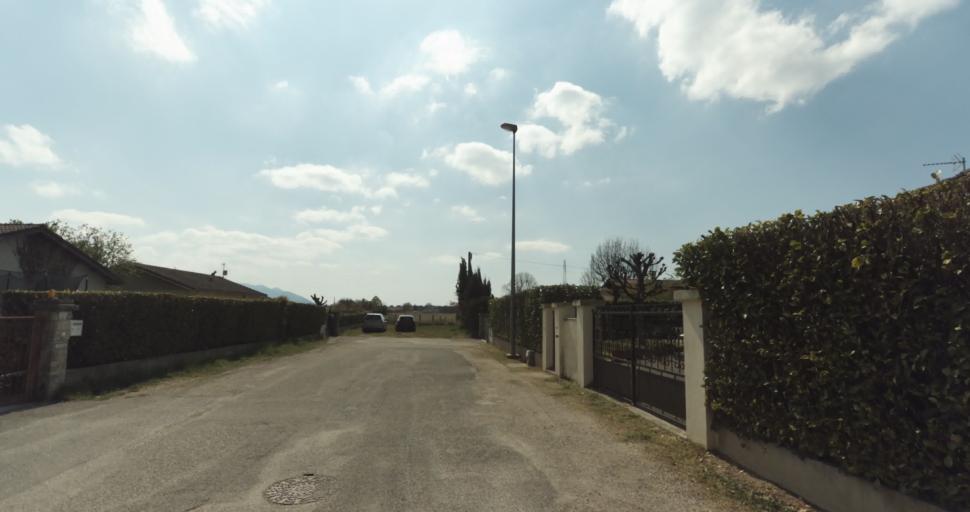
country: FR
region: Rhone-Alpes
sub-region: Departement de l'Isere
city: Saint-Marcellin
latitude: 45.1429
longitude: 5.3140
